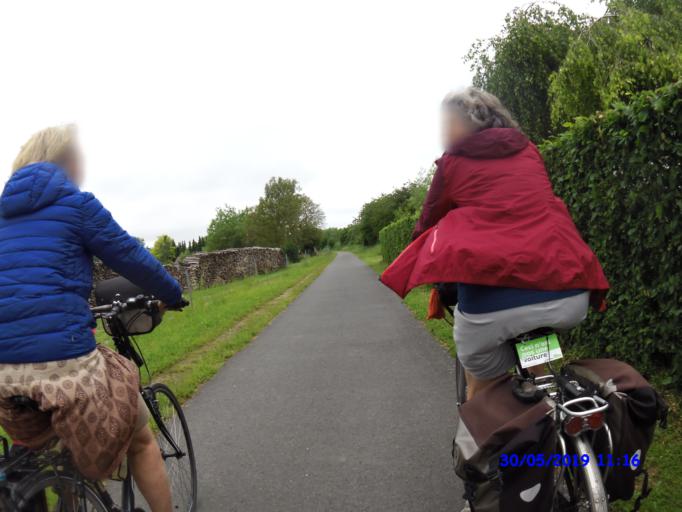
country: BE
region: Wallonia
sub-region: Province du Hainaut
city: Thuin
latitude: 50.3045
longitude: 4.3284
